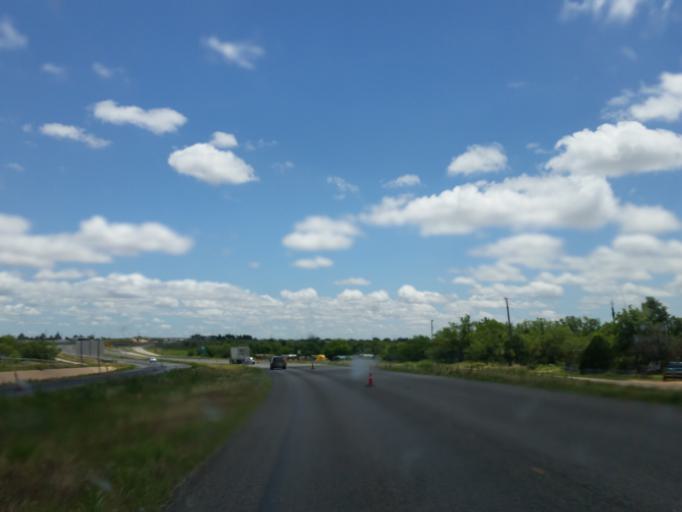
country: US
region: Texas
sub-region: Scurry County
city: Snyder
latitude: 32.7352
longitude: -100.9132
